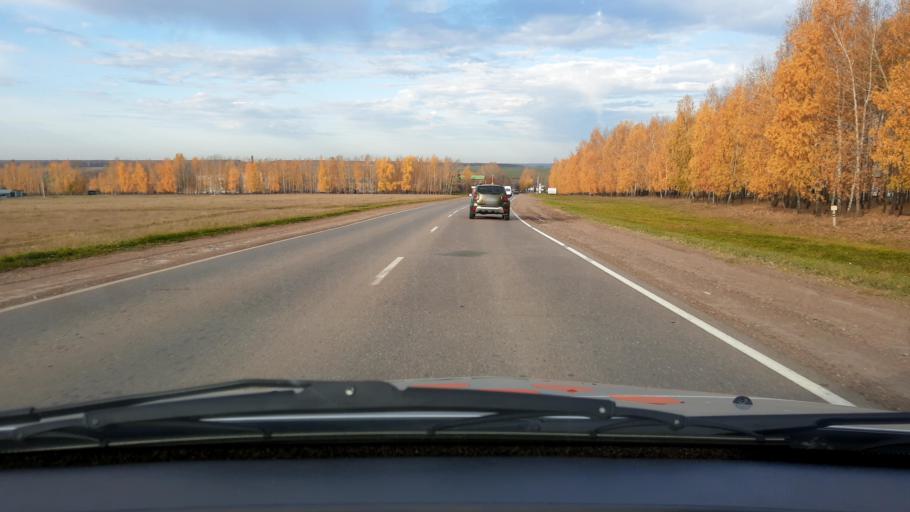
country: RU
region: Bashkortostan
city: Avdon
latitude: 54.8199
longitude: 55.7079
